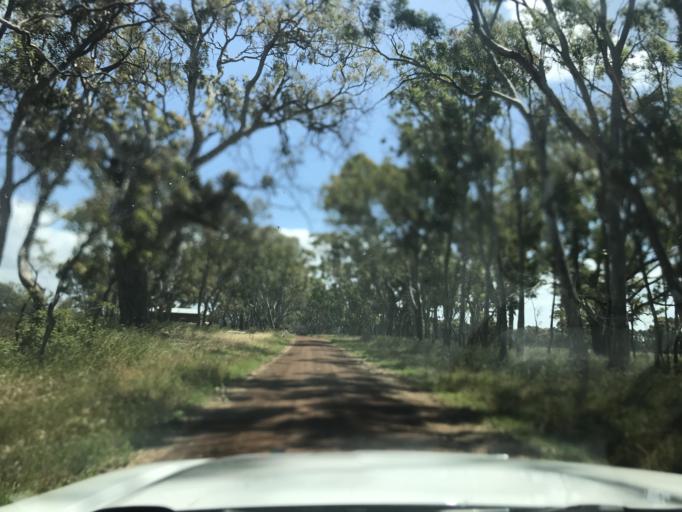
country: AU
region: South Australia
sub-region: Wattle Range
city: Penola
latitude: -37.2863
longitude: 141.4954
